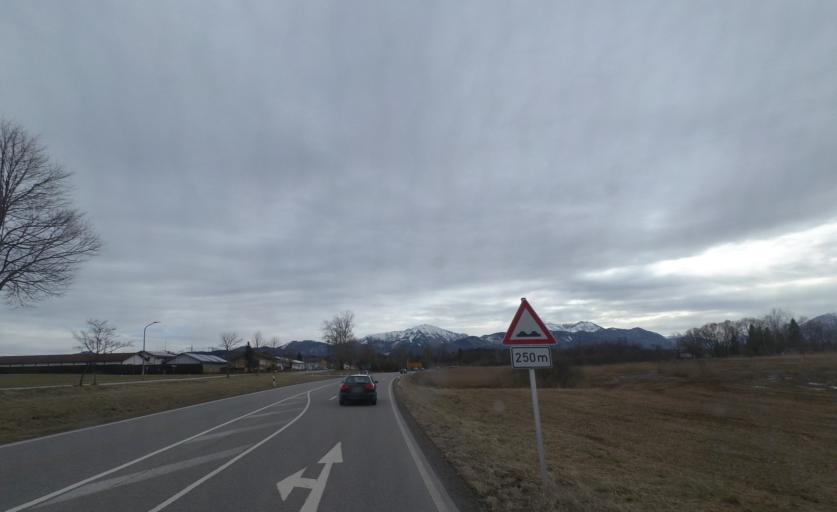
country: DE
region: Bavaria
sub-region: Upper Bavaria
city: Grabenstatt
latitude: 47.8520
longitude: 12.5406
